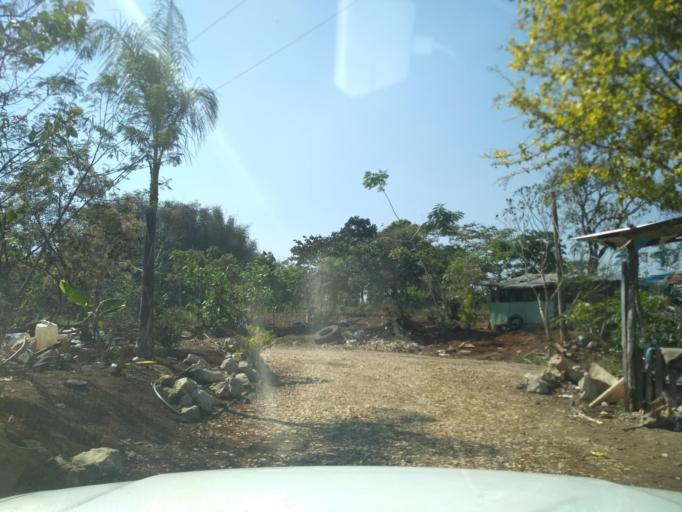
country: MX
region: Veracruz
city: Amatlan de los Reyes
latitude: 18.8483
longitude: -96.9040
